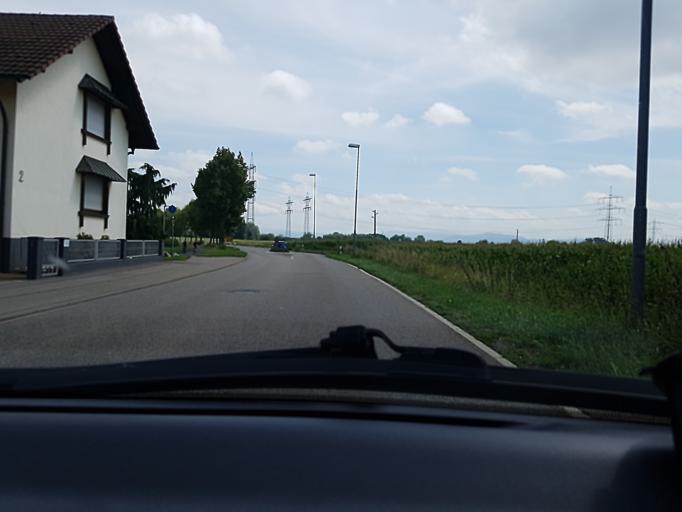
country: DE
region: Baden-Wuerttemberg
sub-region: Freiburg Region
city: Kehl
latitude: 48.5674
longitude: 7.8525
